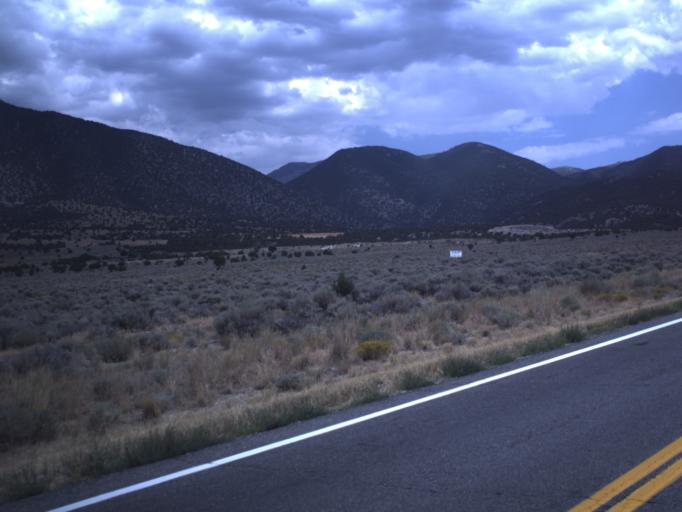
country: US
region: Utah
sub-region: Tooele County
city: Tooele
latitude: 40.3569
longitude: -112.3179
